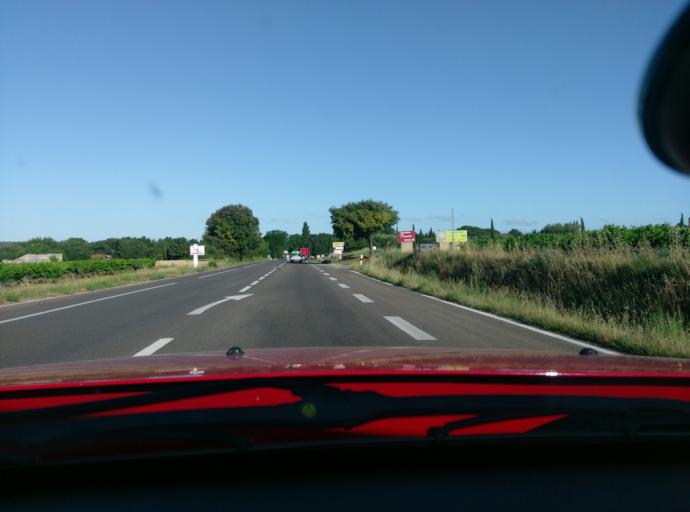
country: FR
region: Languedoc-Roussillon
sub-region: Departement du Gard
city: Uzes
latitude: 43.9898
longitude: 4.4379
